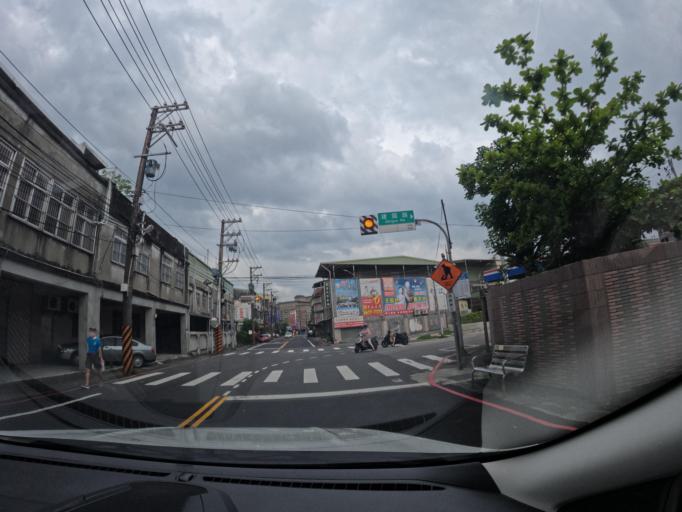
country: TW
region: Taiwan
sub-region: Taoyuan
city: Taoyuan
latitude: 24.9532
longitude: 121.3406
